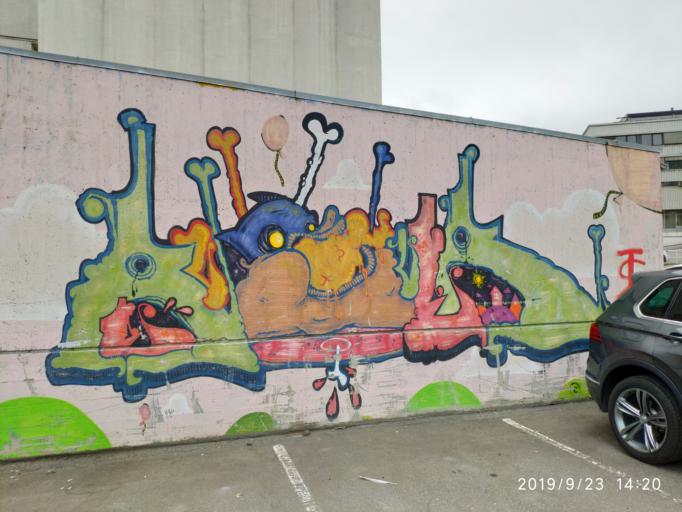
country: NO
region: Oppland
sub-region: Gjovik
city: Gjovik
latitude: 60.7942
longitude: 10.6894
